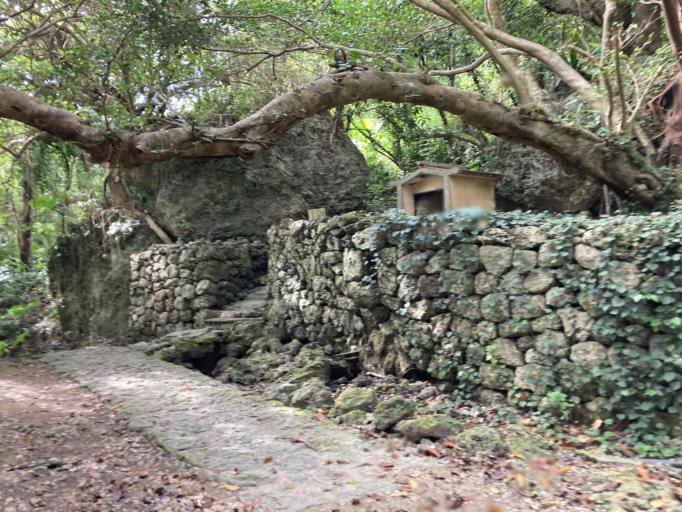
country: JP
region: Okinawa
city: Tomigusuku
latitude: 26.1401
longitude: 127.7963
